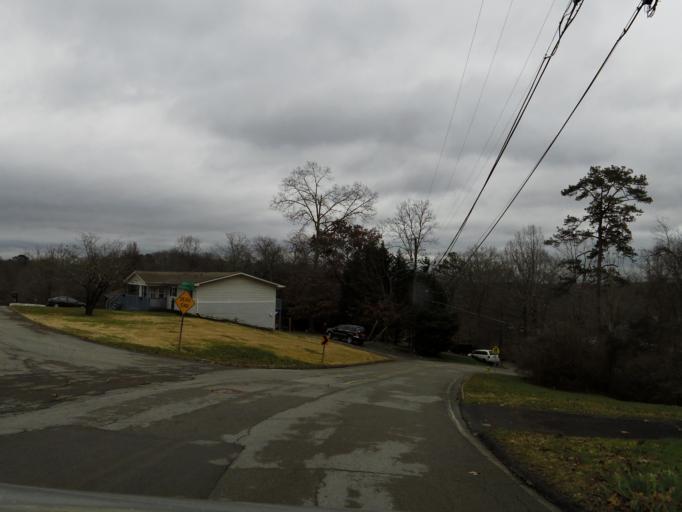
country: US
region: Tennessee
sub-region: Knox County
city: Knoxville
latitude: 35.9883
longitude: -84.0319
